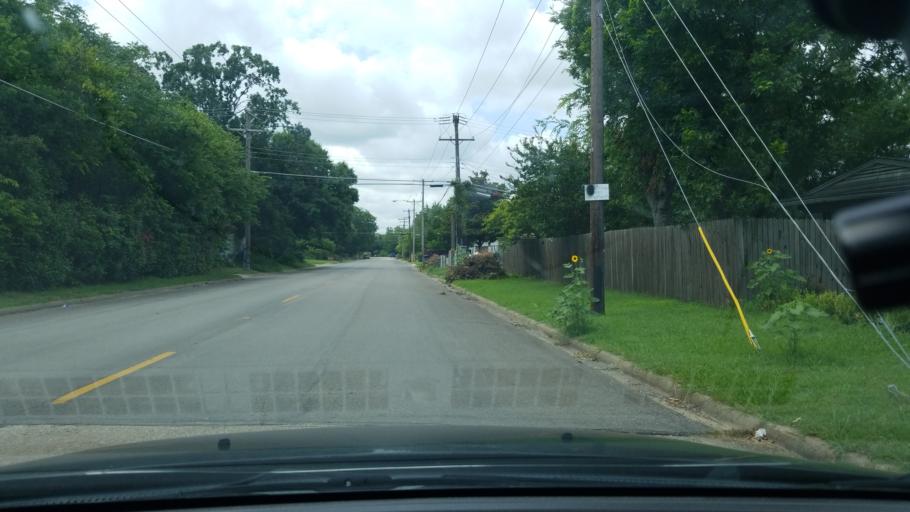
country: US
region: Texas
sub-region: Dallas County
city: Mesquite
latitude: 32.8141
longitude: -96.6733
